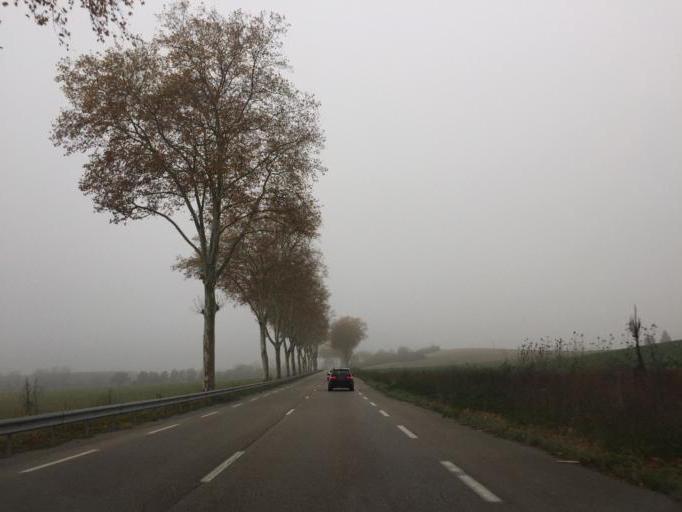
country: FR
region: Rhone-Alpes
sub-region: Departement de l'Ain
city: Mionnay
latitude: 45.8900
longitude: 4.9258
